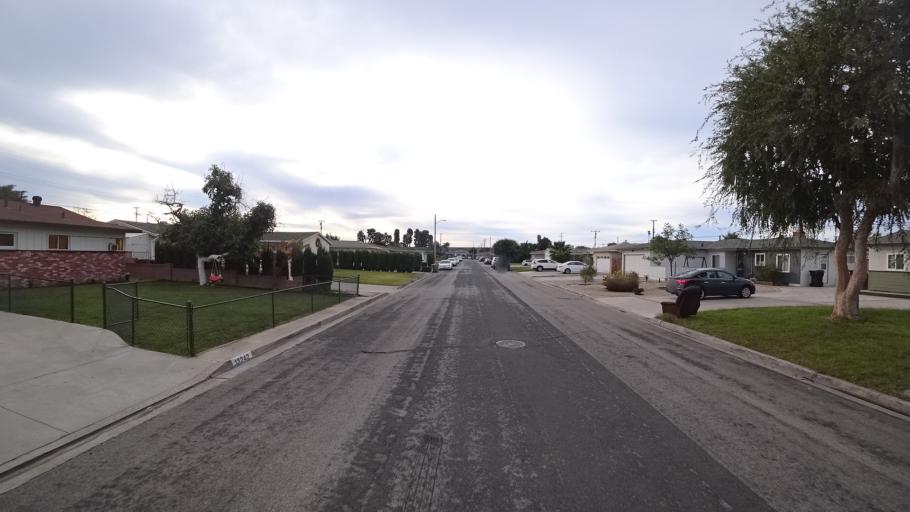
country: US
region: California
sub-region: Orange County
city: Garden Grove
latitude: 33.7707
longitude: -117.9225
